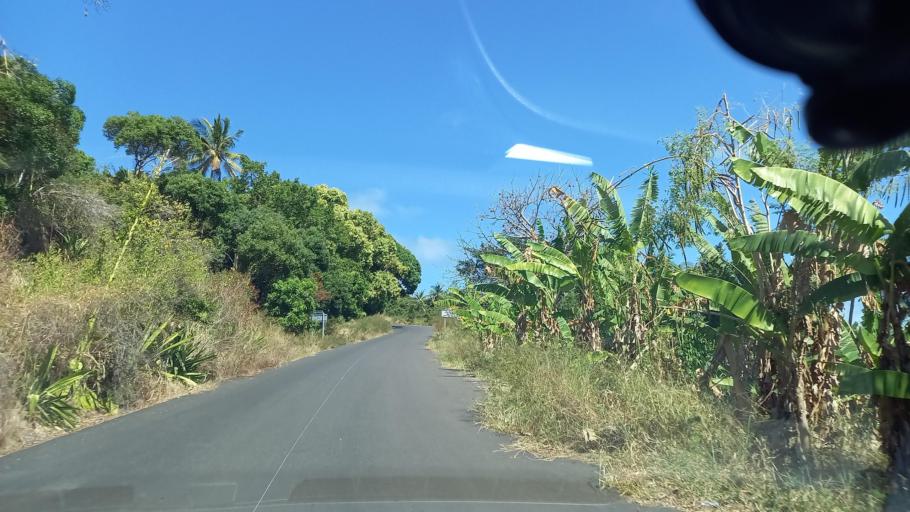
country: YT
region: Kani-Keli
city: Kani Keli
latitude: -12.9673
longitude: 45.1115
